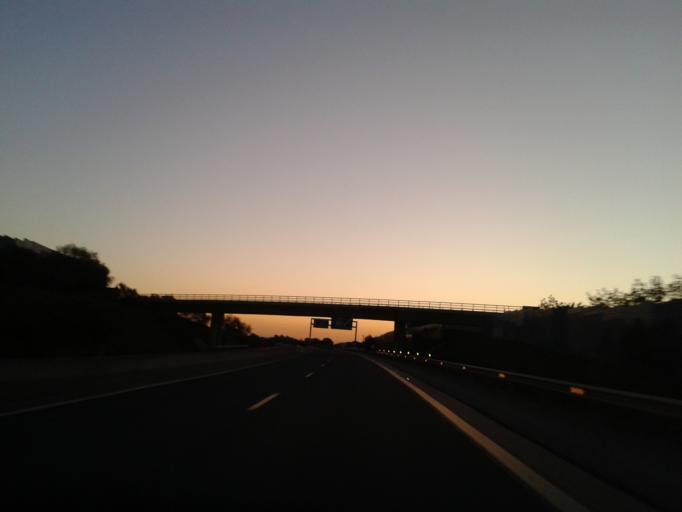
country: PT
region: Faro
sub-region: Albufeira
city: Guia
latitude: 37.1388
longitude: -8.2724
